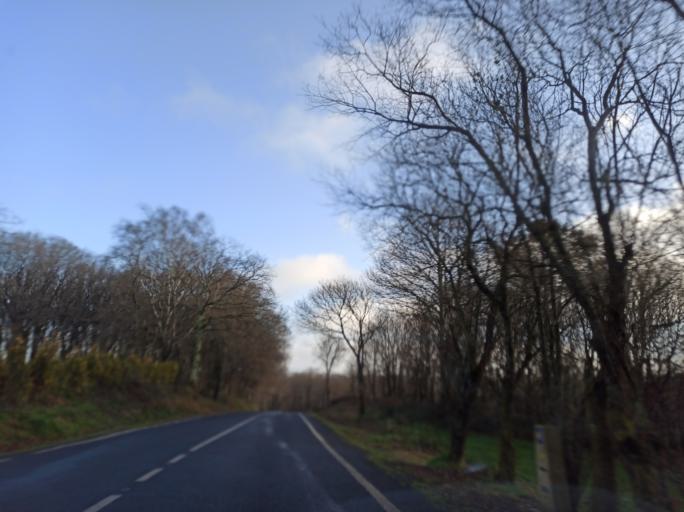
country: ES
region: Galicia
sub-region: Provincia da Coruna
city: Curtis
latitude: 43.0908
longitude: -7.9952
